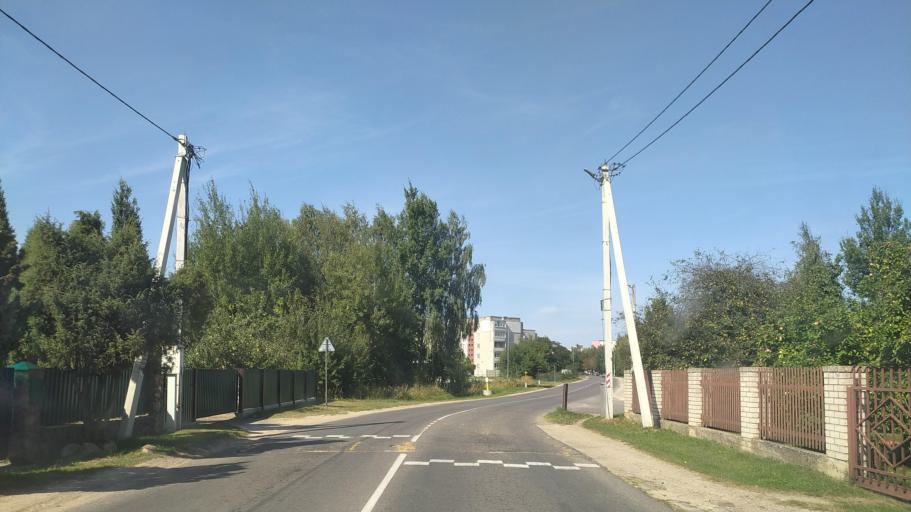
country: BY
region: Brest
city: Byaroza
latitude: 52.5342
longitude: 24.9953
